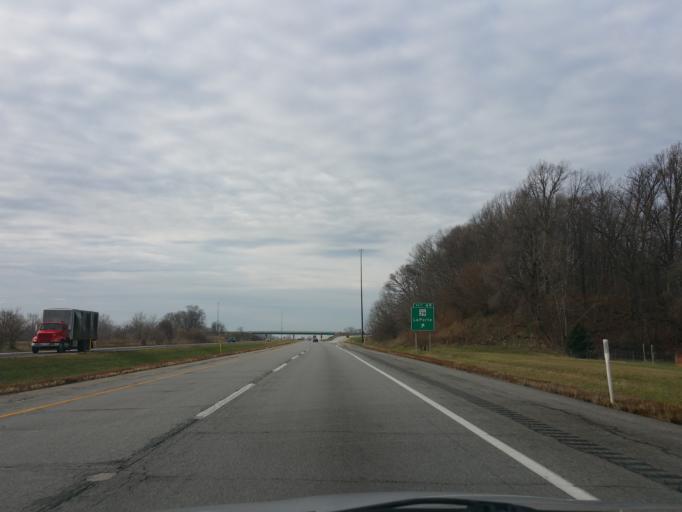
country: US
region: Indiana
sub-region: LaPorte County
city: LaPorte
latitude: 41.6691
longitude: -86.7250
